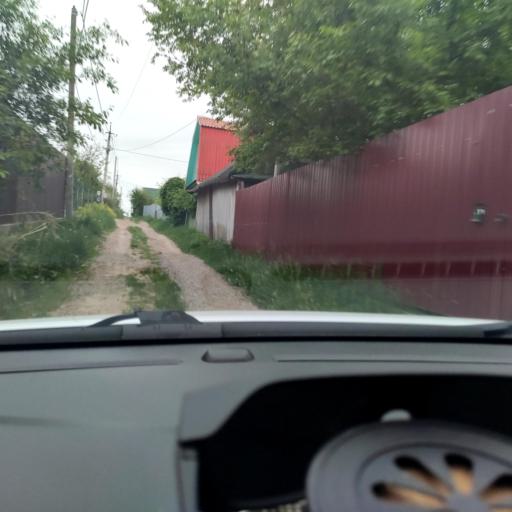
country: RU
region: Tatarstan
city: Vysokaya Gora
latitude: 55.8531
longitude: 49.2487
